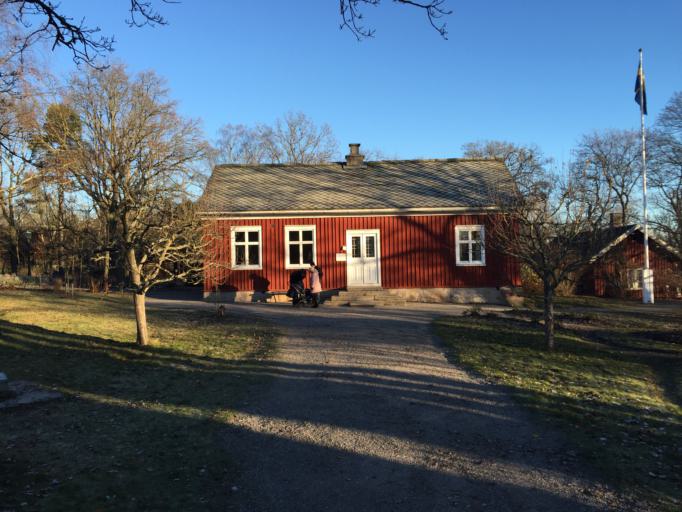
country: SE
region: Stockholm
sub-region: Stockholms Kommun
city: OEstermalm
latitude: 59.3251
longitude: 18.1064
